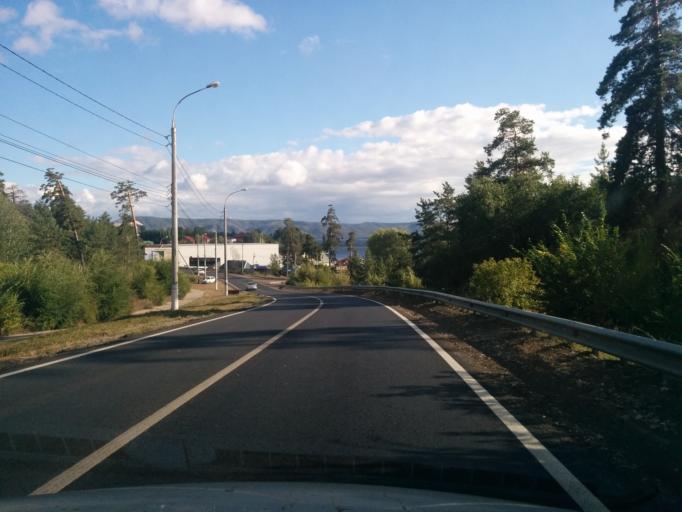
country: RU
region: Samara
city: Tol'yatti
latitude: 53.4788
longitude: 49.3228
